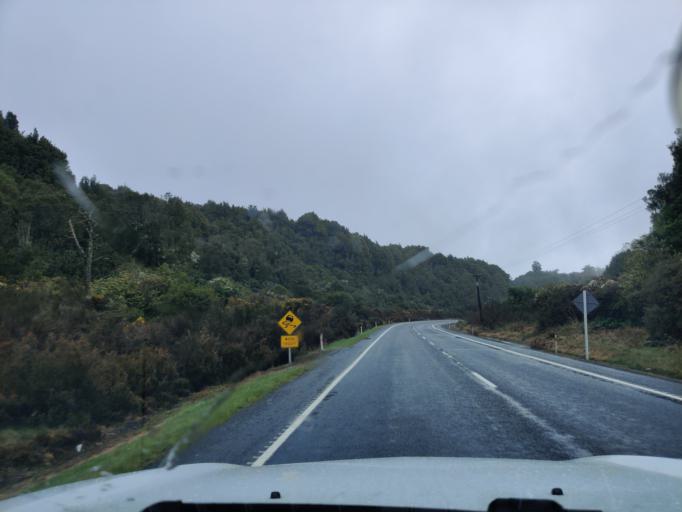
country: NZ
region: Bay of Plenty
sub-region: Rotorua District
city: Rotorua
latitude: -38.0349
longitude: 176.0232
